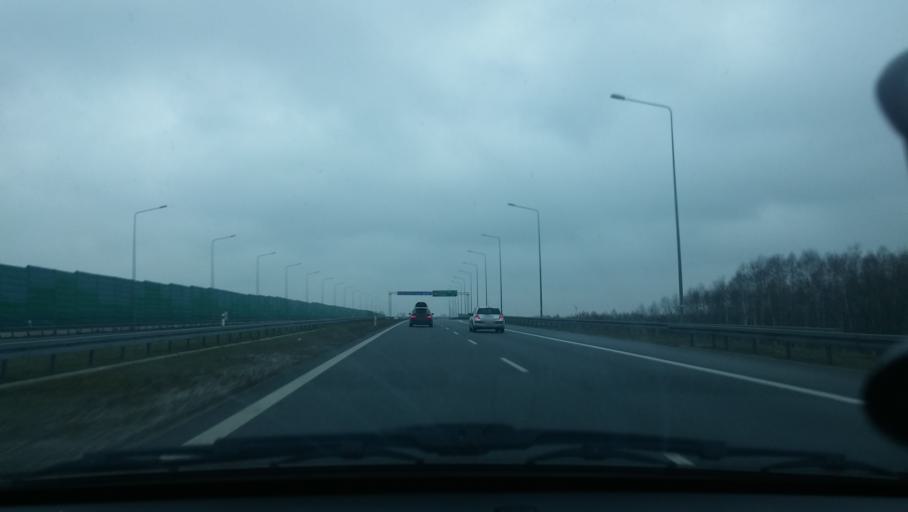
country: PL
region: Masovian Voivodeship
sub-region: Powiat minski
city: Minsk Mazowiecki
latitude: 52.2067
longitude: 21.5191
